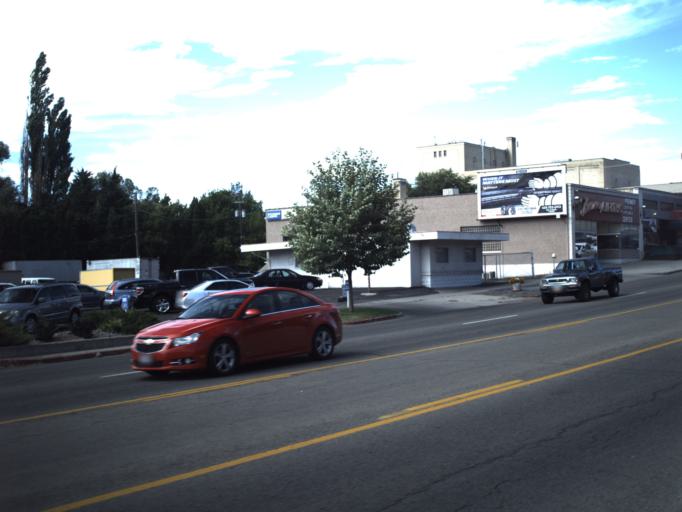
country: US
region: Utah
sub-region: Cache County
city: Logan
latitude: 41.7289
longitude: -111.8350
